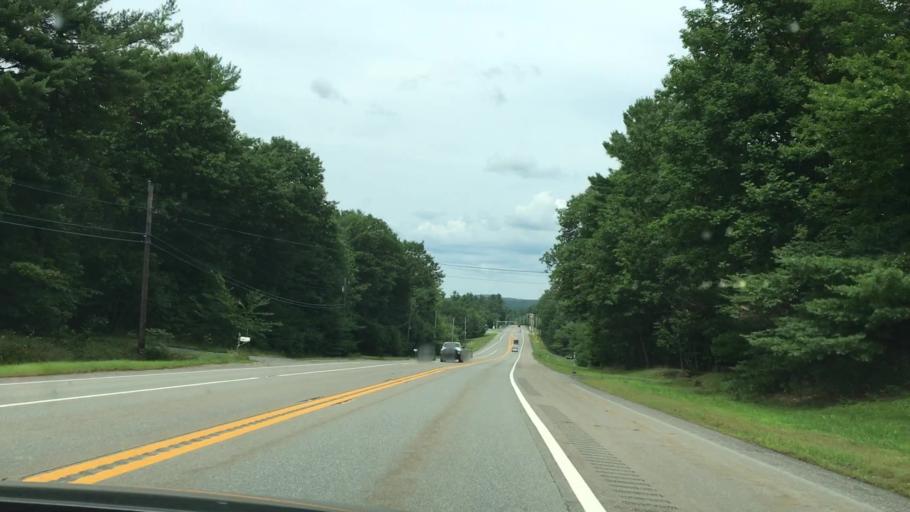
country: US
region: Massachusetts
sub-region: Worcester County
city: Gardner
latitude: 42.6355
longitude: -72.0064
